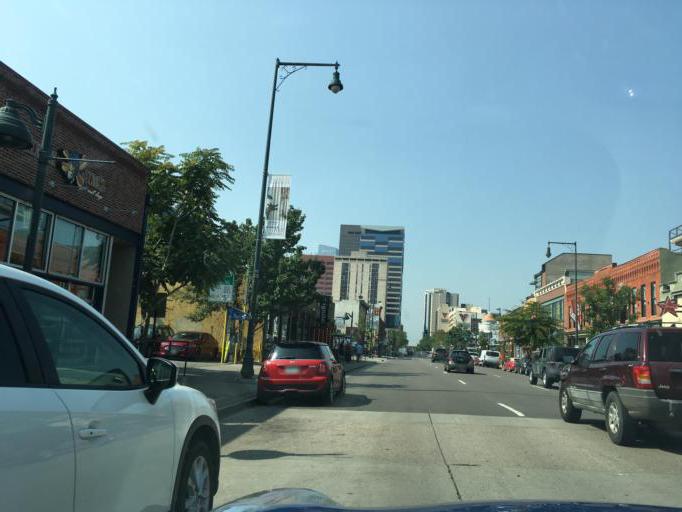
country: US
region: Colorado
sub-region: Denver County
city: Denver
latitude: 39.7546
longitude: -104.9904
